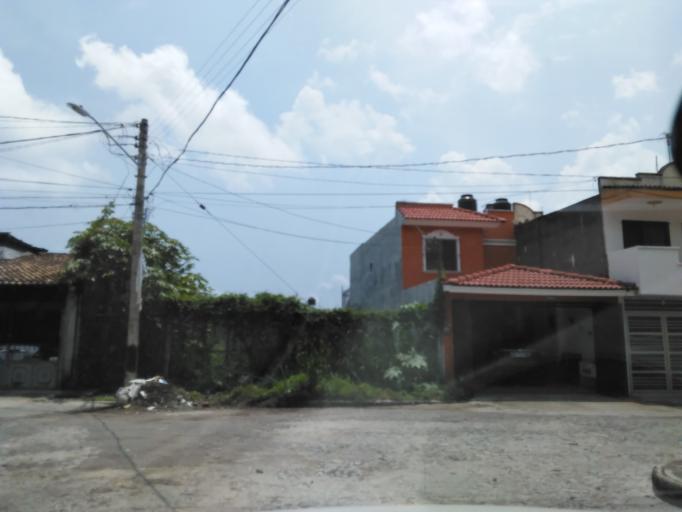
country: MX
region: Nayarit
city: Tepic
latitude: 21.5090
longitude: -104.9185
